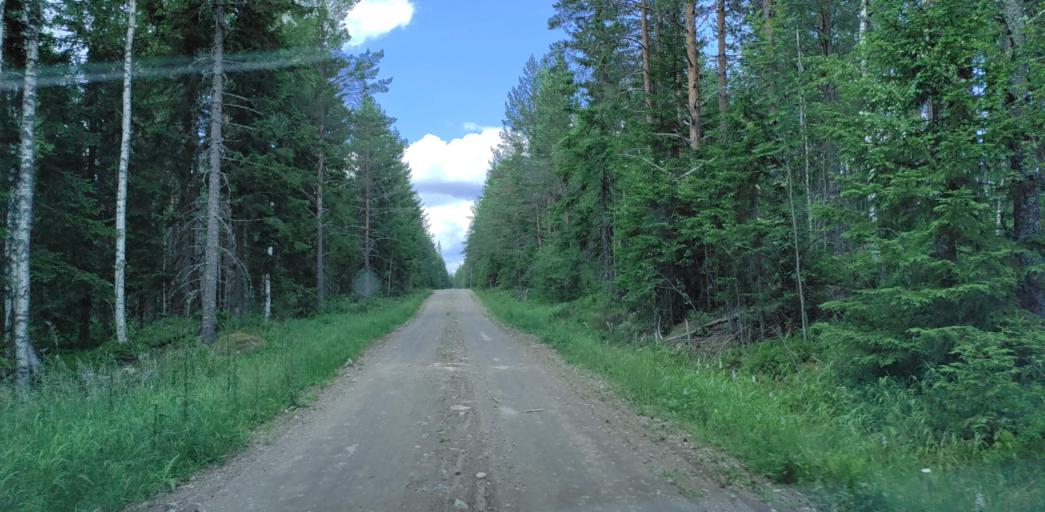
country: SE
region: Vaermland
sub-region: Hagfors Kommun
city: Ekshaerad
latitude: 60.0799
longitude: 13.3467
